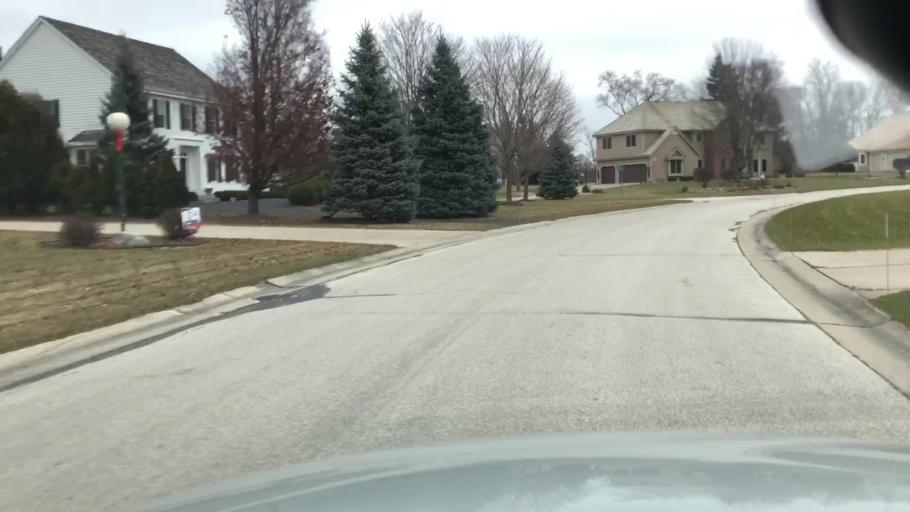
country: US
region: Wisconsin
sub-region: Waukesha County
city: Brookfield
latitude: 43.0717
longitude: -88.1684
